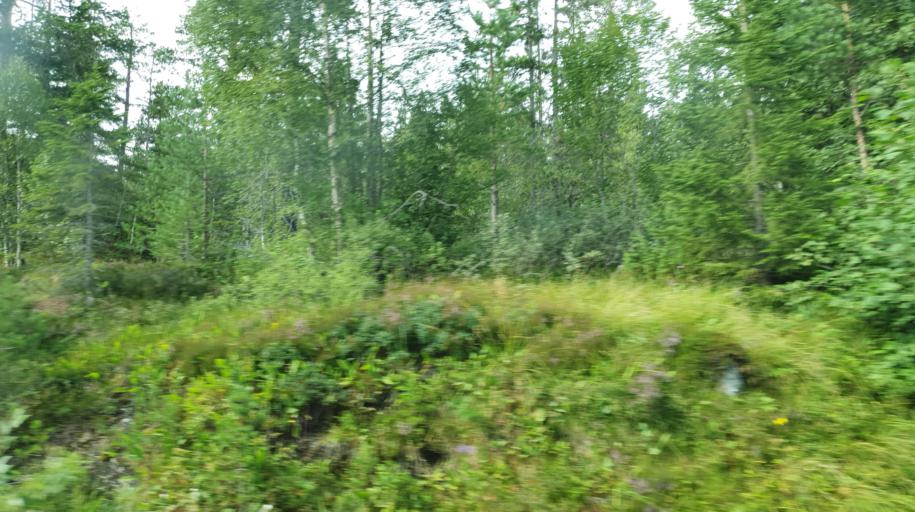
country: NO
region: Nord-Trondelag
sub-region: Levanger
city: Skogn
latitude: 63.5749
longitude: 11.2188
